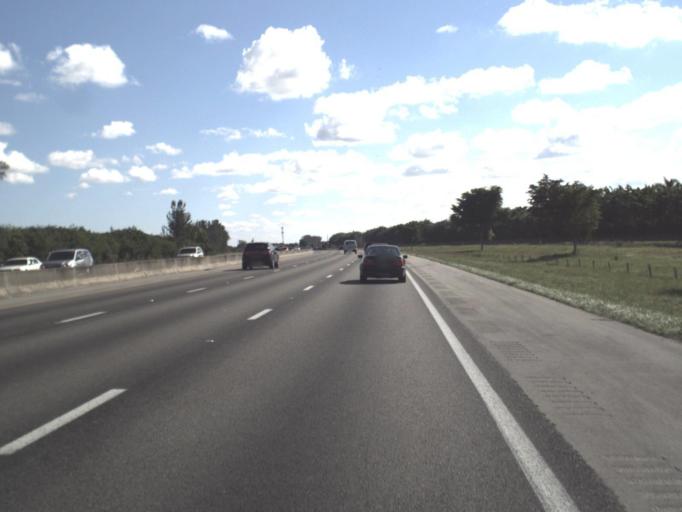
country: US
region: Florida
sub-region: Palm Beach County
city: Villages of Oriole
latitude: 26.4413
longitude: -80.1744
